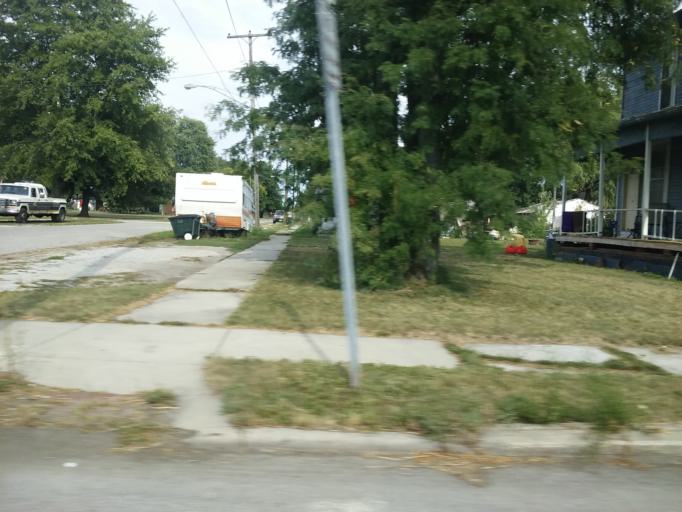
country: US
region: Ohio
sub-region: Hancock County
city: McComb
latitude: 41.1908
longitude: -83.7844
